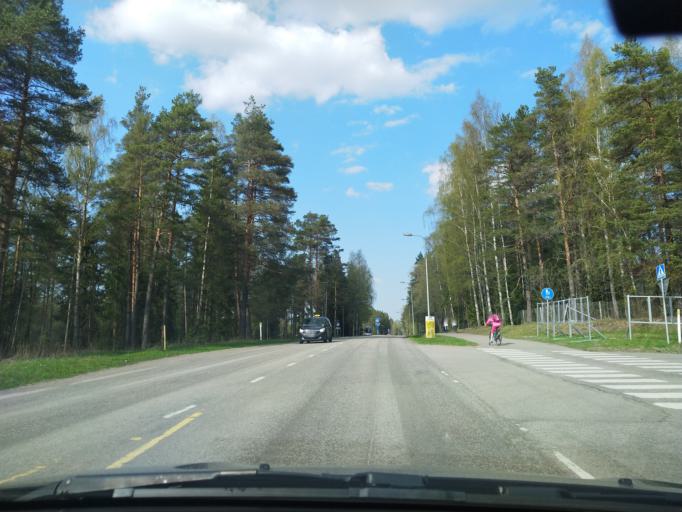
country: FI
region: Uusimaa
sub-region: Helsinki
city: Lohja
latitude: 60.1835
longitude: 23.9940
